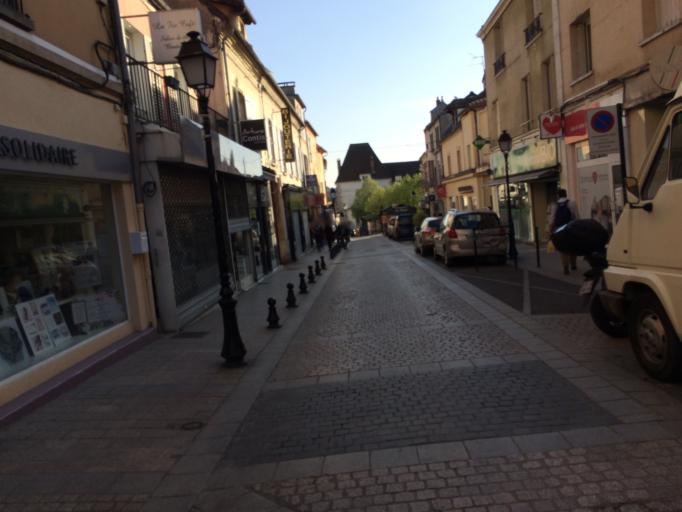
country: FR
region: Ile-de-France
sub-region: Departement de l'Essonne
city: Palaiseau
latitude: 48.7129
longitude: 2.2440
